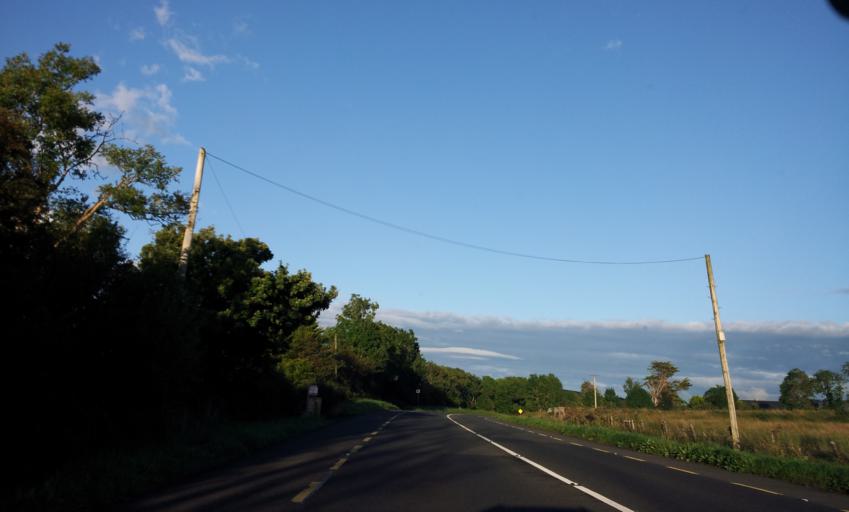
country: IE
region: Munster
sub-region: County Limerick
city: Abbeyfeale
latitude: 52.3876
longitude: -9.2435
